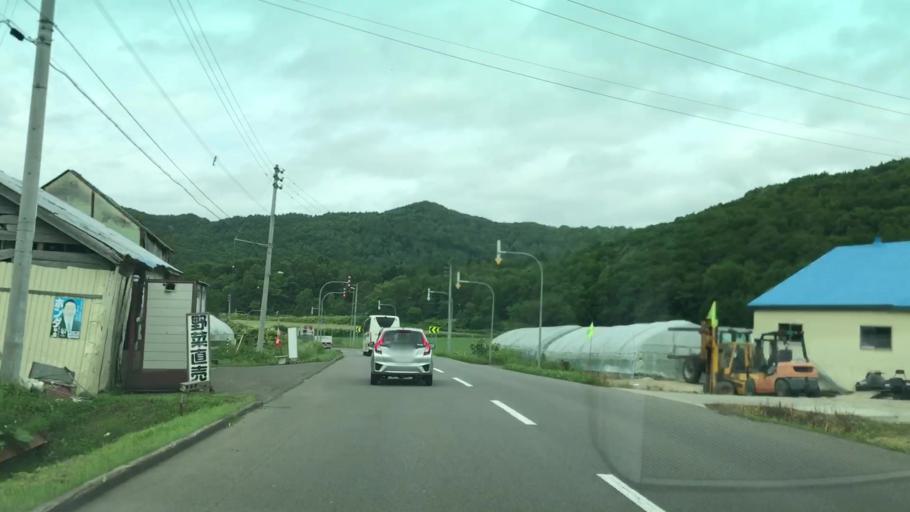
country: JP
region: Hokkaido
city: Niseko Town
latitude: 42.9486
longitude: 140.8319
